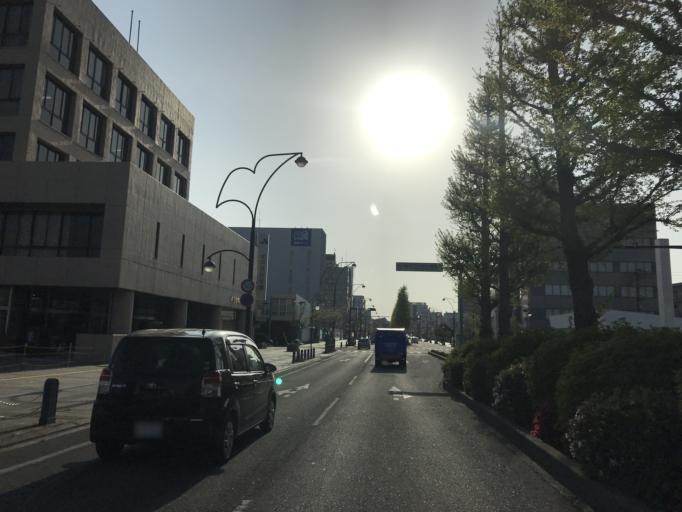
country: JP
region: Ibaraki
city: Hitachi-Naka
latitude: 36.3948
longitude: 140.5310
